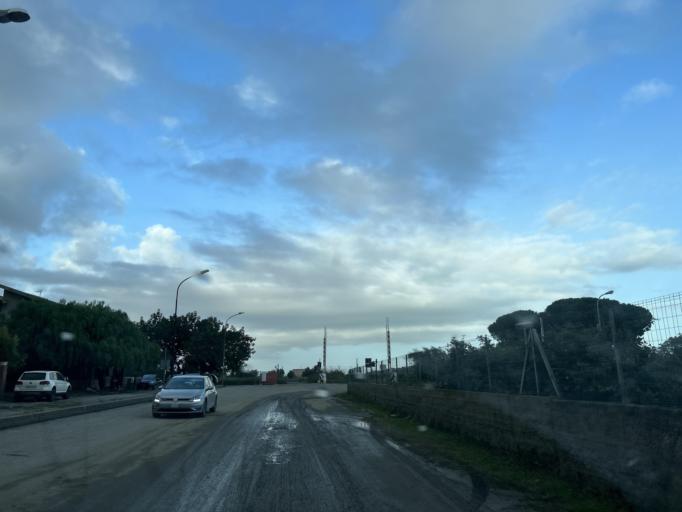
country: IT
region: Calabria
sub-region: Provincia di Catanzaro
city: Squillace Lido
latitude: 38.7791
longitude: 16.5722
